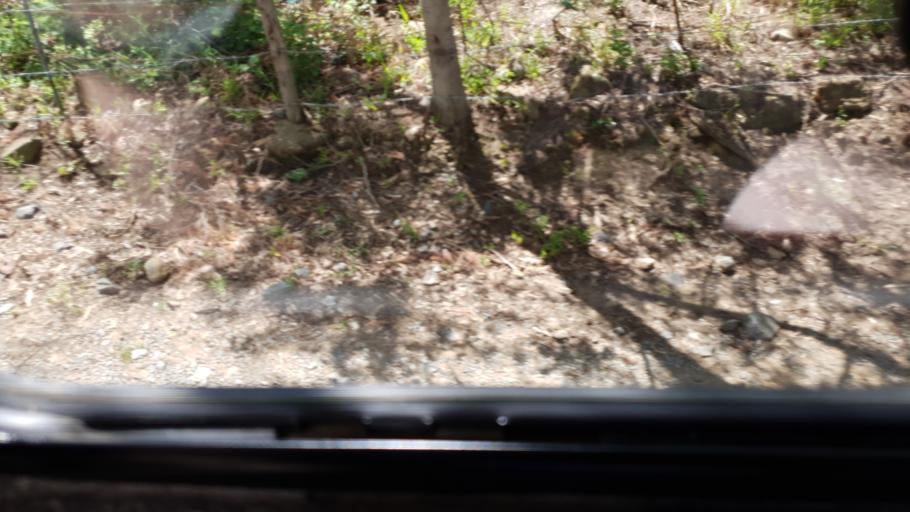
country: LS
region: Maseru
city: Nako
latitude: -29.6286
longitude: 27.5088
